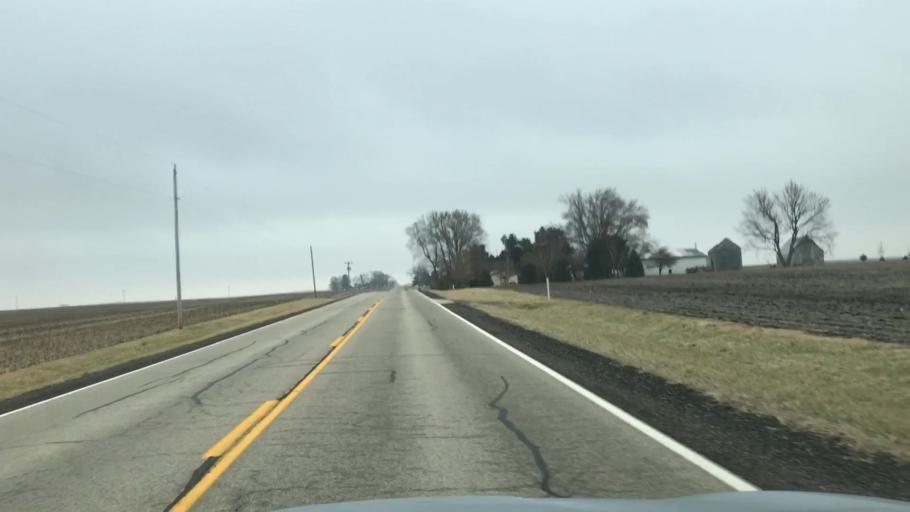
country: US
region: Illinois
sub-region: McLean County
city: Hudson
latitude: 40.6116
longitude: -88.9454
